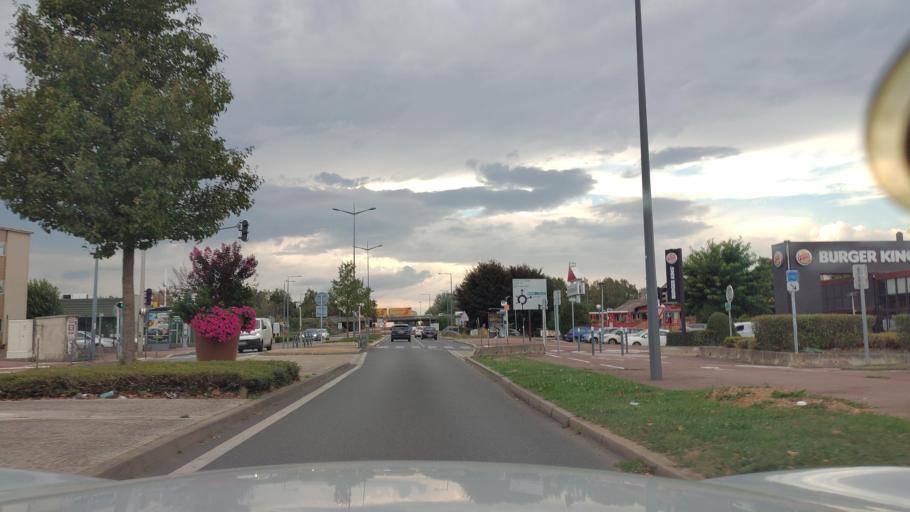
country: FR
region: Ile-de-France
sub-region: Departement de Seine-et-Marne
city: Servon
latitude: 48.7018
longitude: 2.5989
